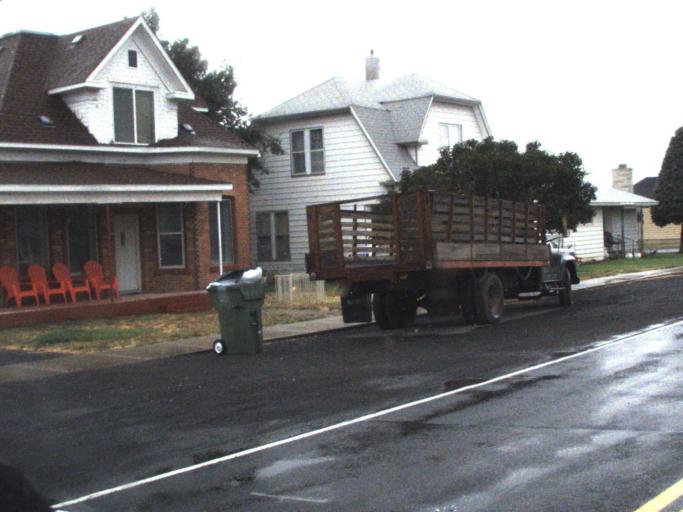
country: US
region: Washington
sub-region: Lincoln County
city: Davenport
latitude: 47.4822
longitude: -118.2546
